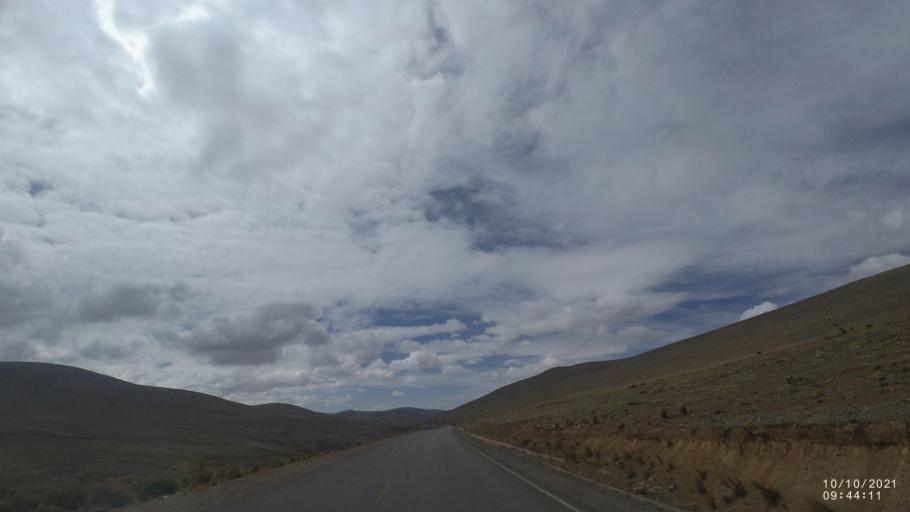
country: BO
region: La Paz
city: Quime
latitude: -17.1577
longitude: -67.3403
